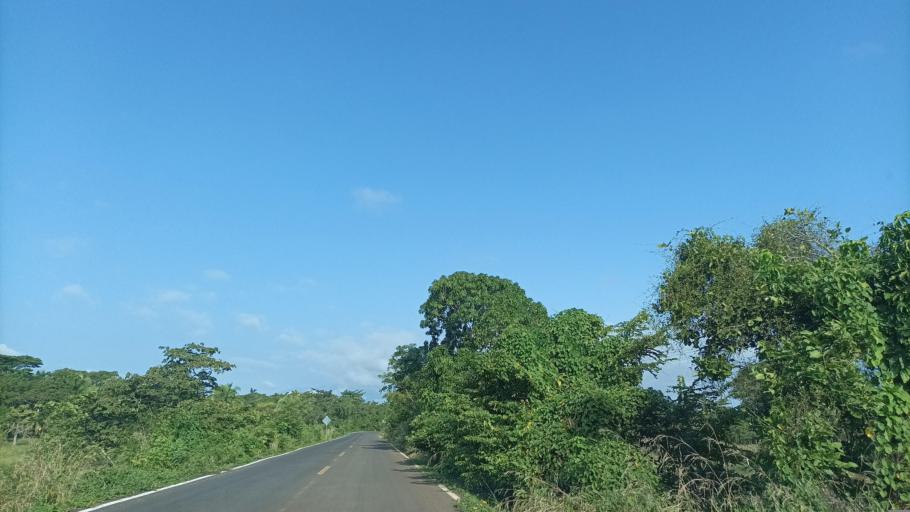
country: MX
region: Veracruz
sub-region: Chinameca
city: Chacalapa
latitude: 18.1391
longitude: -94.6515
